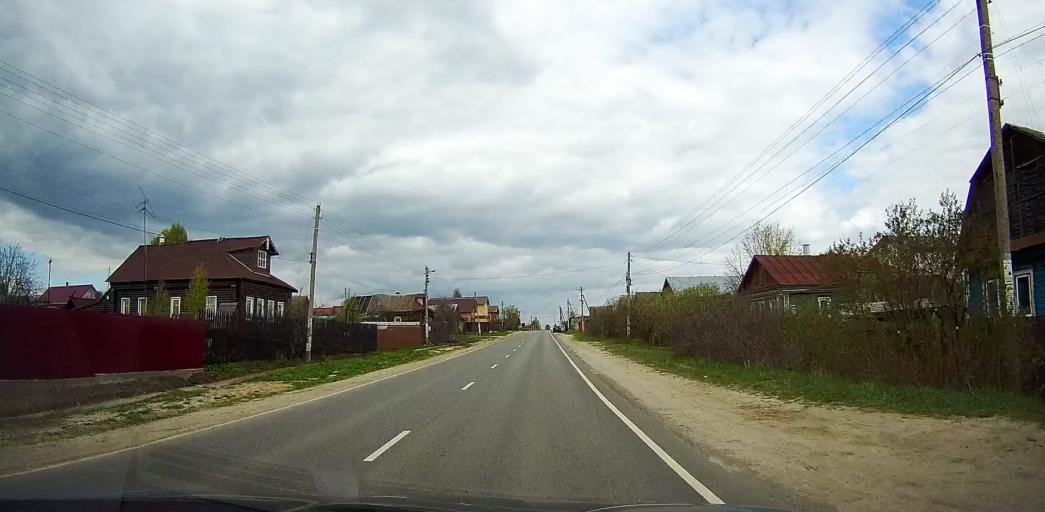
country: RU
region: Moskovskaya
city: Ashitkovo
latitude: 55.4516
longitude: 38.5937
